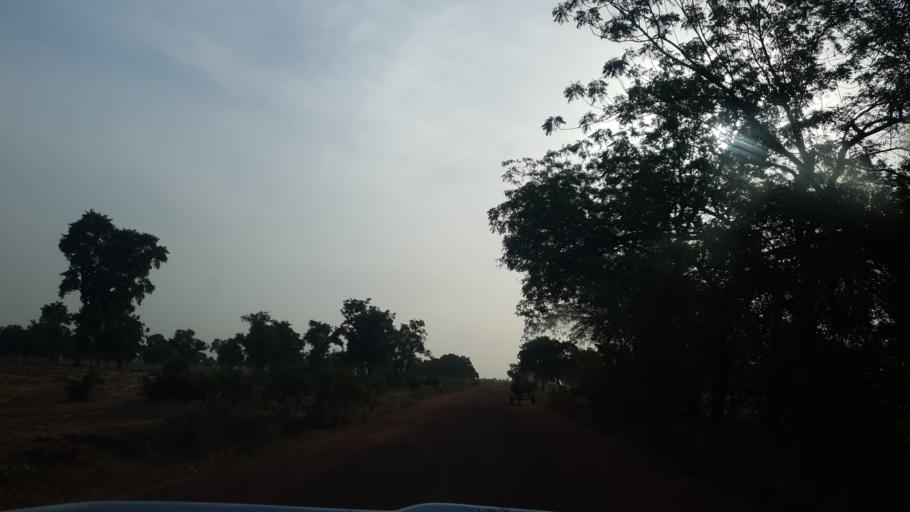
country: ML
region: Koulikoro
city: Dioila
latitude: 12.7702
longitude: -6.9300
